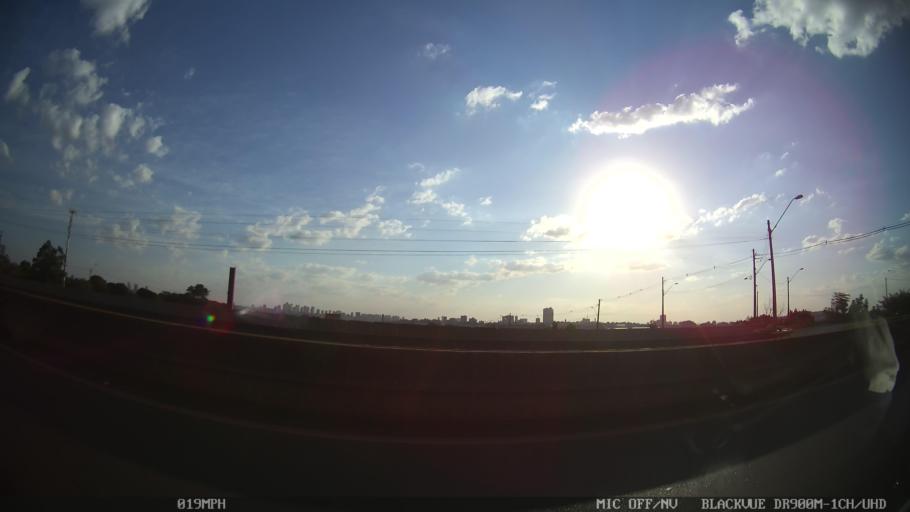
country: BR
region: Sao Paulo
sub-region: Ribeirao Preto
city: Ribeirao Preto
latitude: -21.2064
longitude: -47.7496
